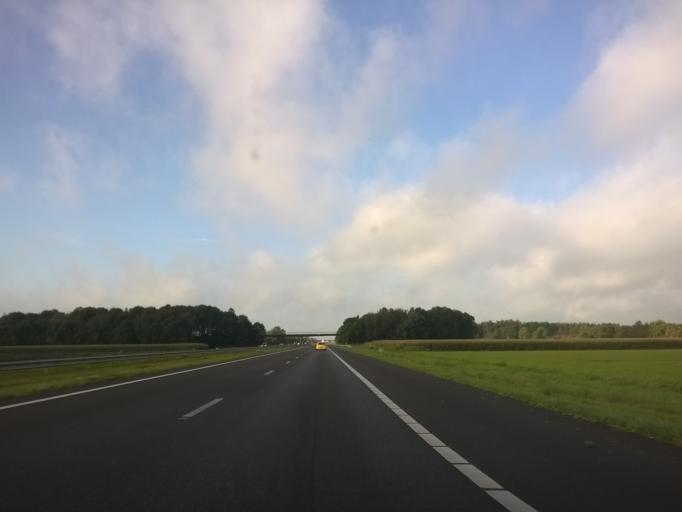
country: NL
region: Friesland
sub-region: Gemeente Achtkarspelen
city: Surhuisterveen
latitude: 53.1401
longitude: 6.2209
